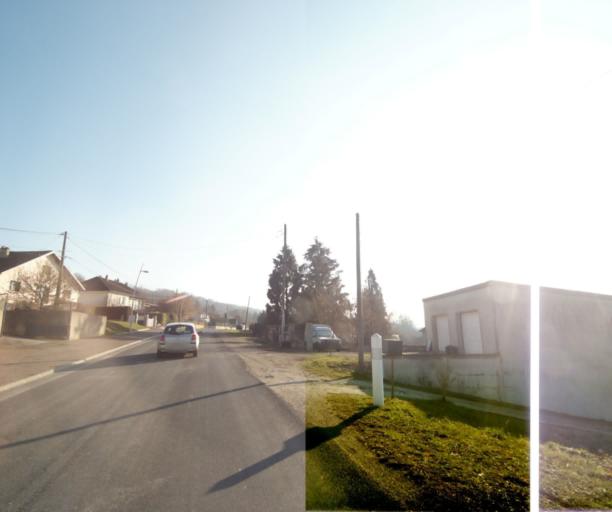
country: FR
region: Champagne-Ardenne
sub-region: Departement de la Haute-Marne
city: Chevillon
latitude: 48.5217
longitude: 5.1168
